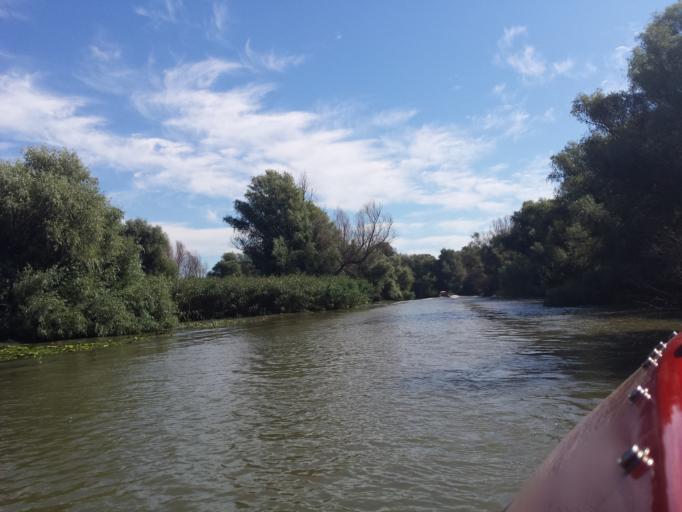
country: RO
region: Tulcea
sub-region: Comuna Mahmudia
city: Mahmudia
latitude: 45.2365
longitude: 29.1117
